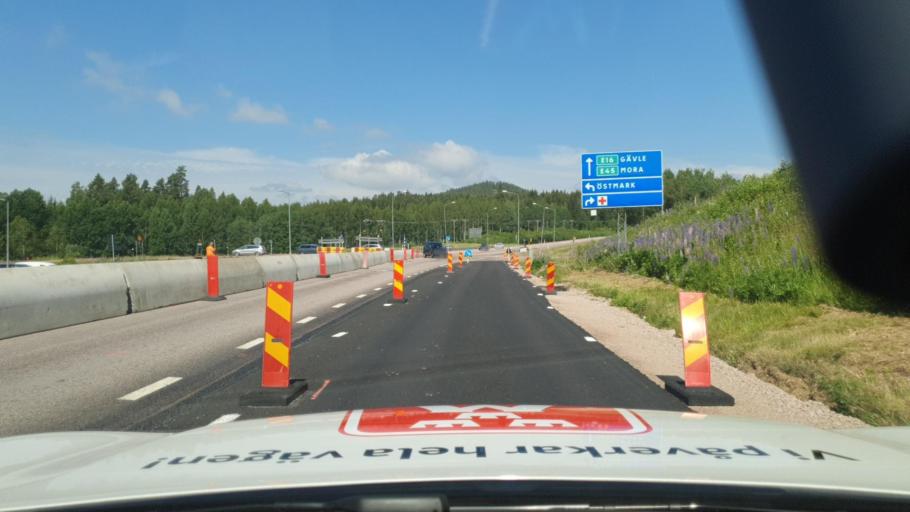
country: SE
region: Vaermland
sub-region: Torsby Kommun
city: Torsby
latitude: 60.1363
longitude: 12.9879
